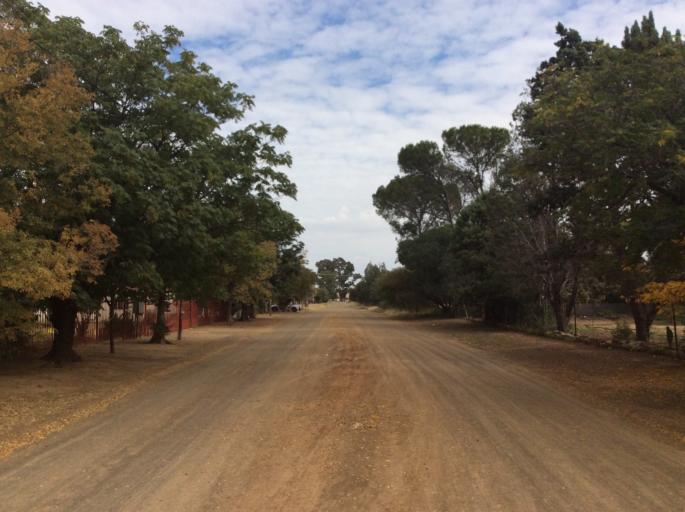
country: LS
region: Mafeteng
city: Mafeteng
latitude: -29.7301
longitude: 27.0296
